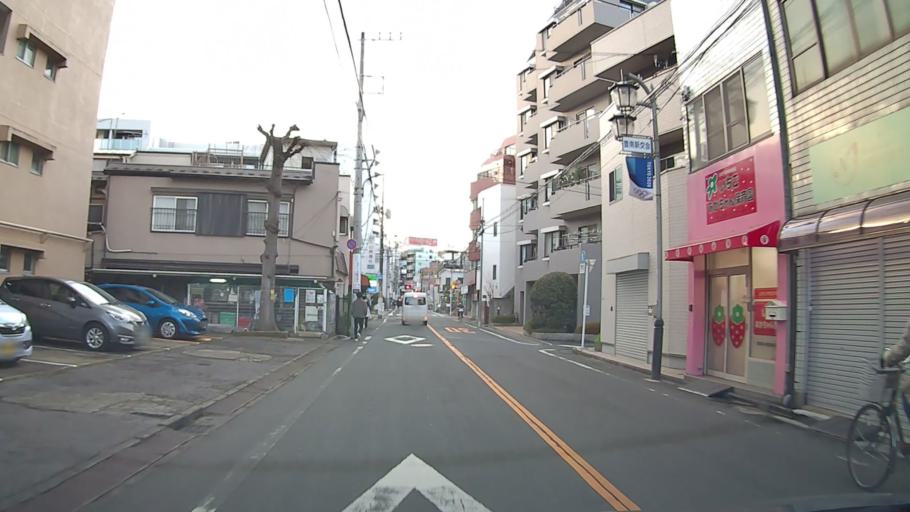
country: JP
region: Tokyo
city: Tokyo
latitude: 35.7372
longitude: 139.6581
